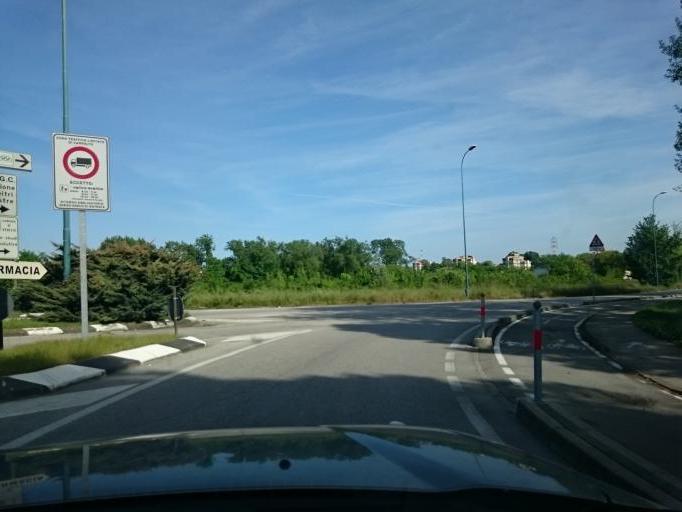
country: IT
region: Veneto
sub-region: Provincia di Venezia
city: Campalto
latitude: 45.4845
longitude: 12.2837
